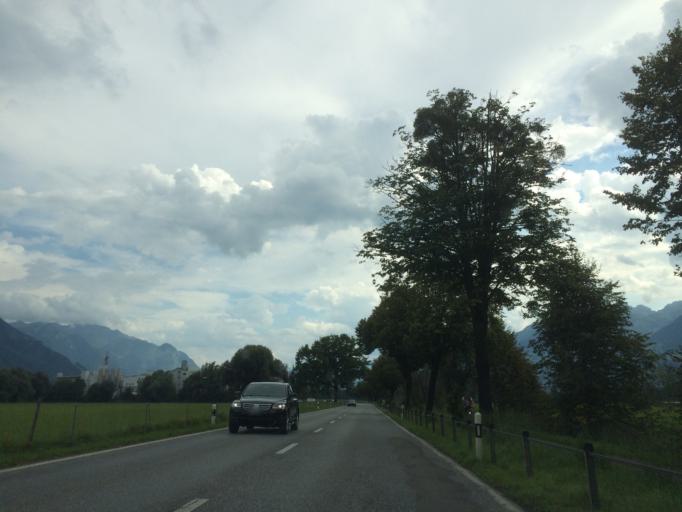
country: CH
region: Saint Gallen
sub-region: Wahlkreis Werdenberg
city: Haag (Rheintal)
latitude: 47.2040
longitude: 9.5014
